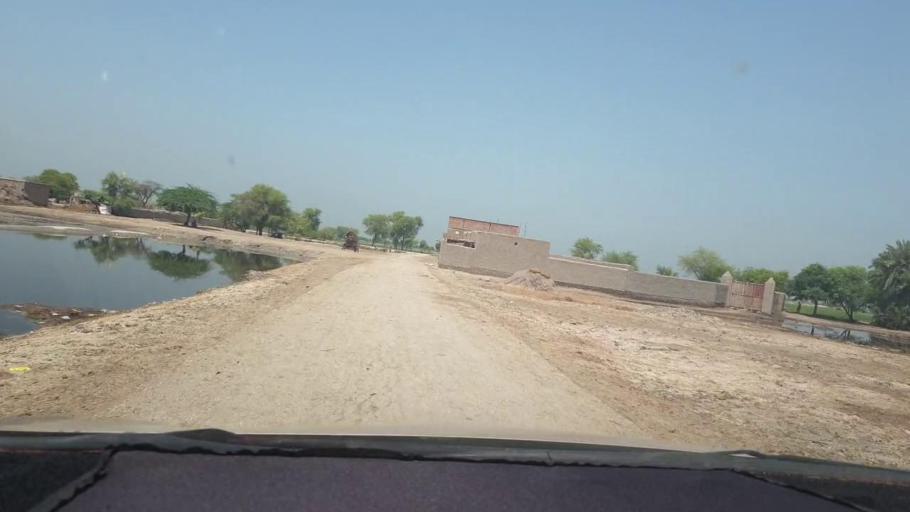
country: PK
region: Sindh
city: Kambar
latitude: 27.6265
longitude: 68.0511
